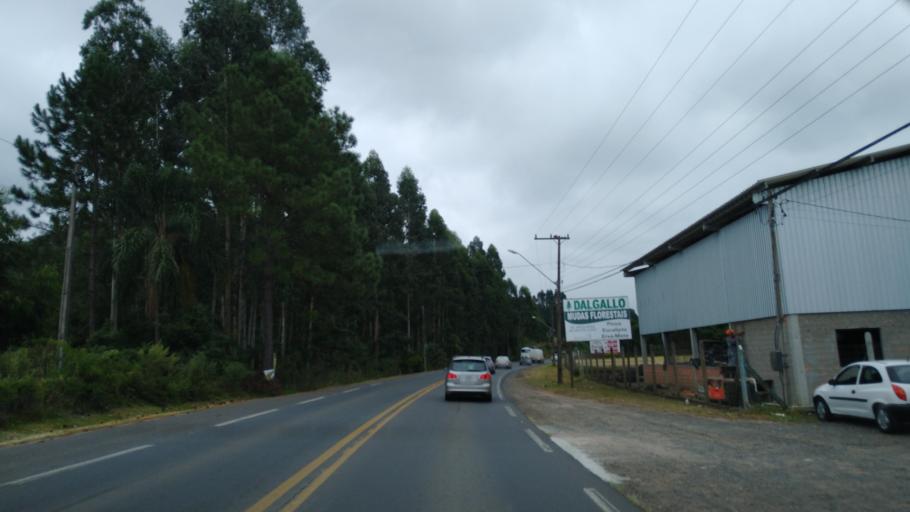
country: BR
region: Santa Catarina
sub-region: Porto Uniao
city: Porto Uniao
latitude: -26.2785
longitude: -51.0527
